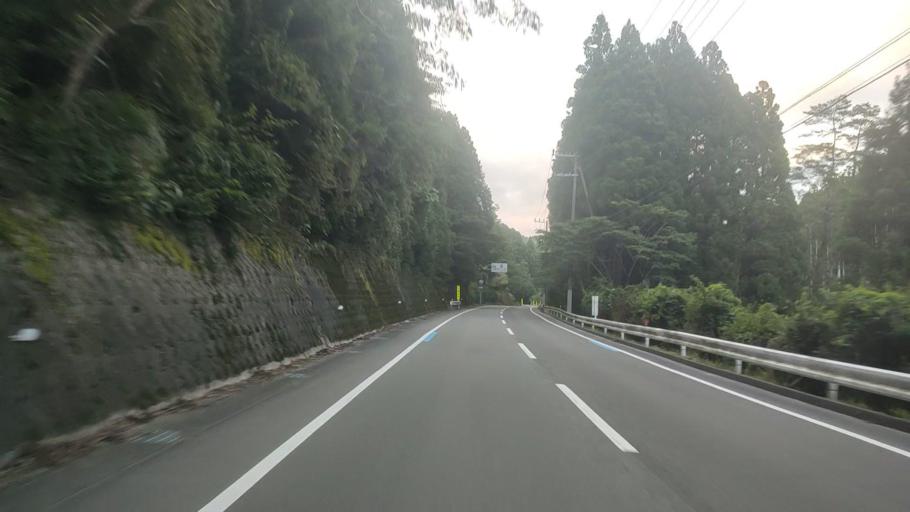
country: JP
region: Wakayama
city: Tanabe
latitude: 33.8291
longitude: 135.6415
